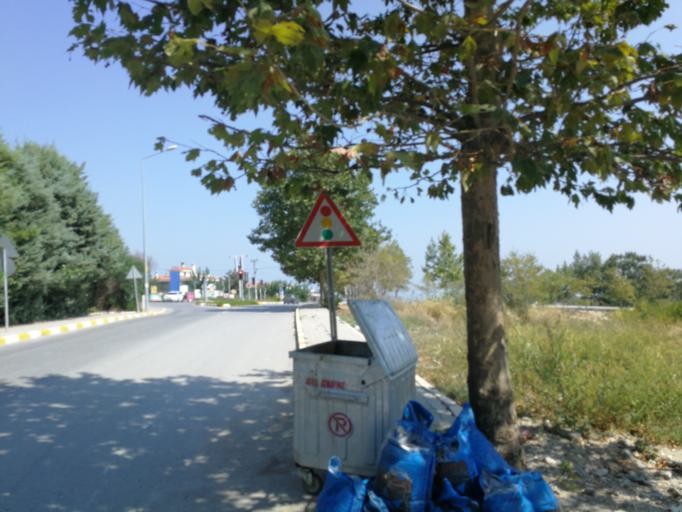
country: TR
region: Izmir
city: Urla
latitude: 38.3260
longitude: 26.7723
